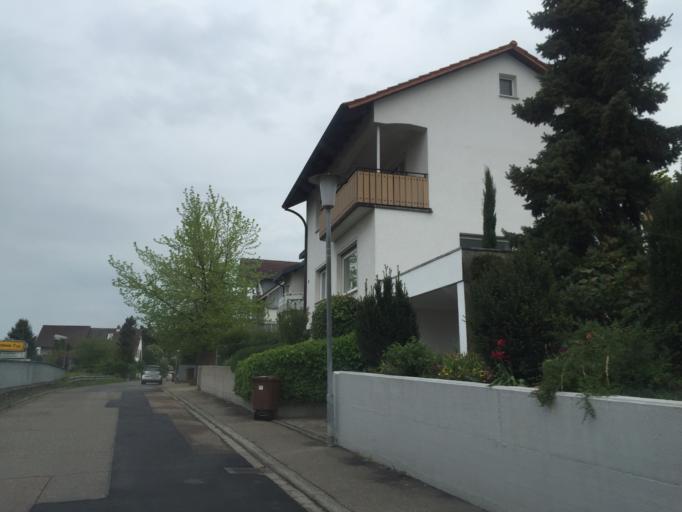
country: DE
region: Baden-Wuerttemberg
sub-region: Karlsruhe Region
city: Weinheim
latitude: 49.5233
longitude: 8.6681
